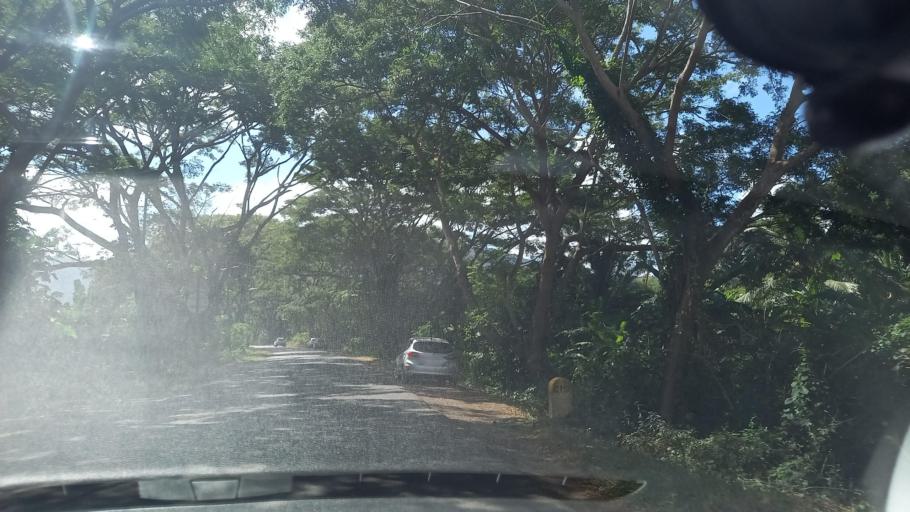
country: YT
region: Chirongui
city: Chirongui
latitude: -12.9183
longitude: 45.1593
